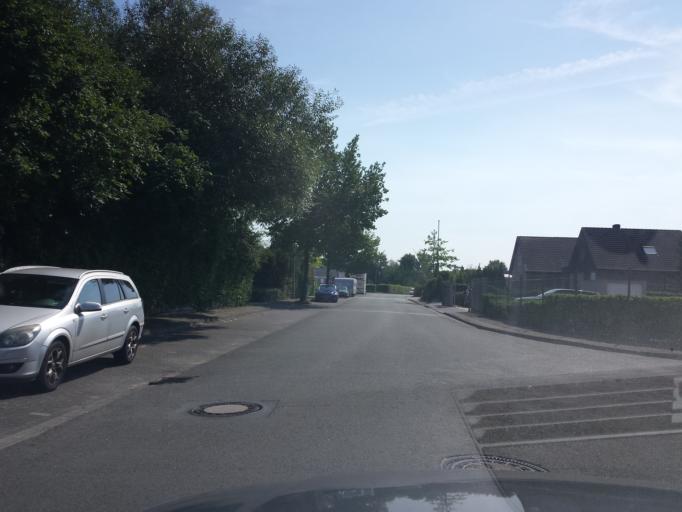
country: DE
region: North Rhine-Westphalia
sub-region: Regierungsbezirk Munster
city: Senden
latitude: 51.8462
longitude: 7.4833
